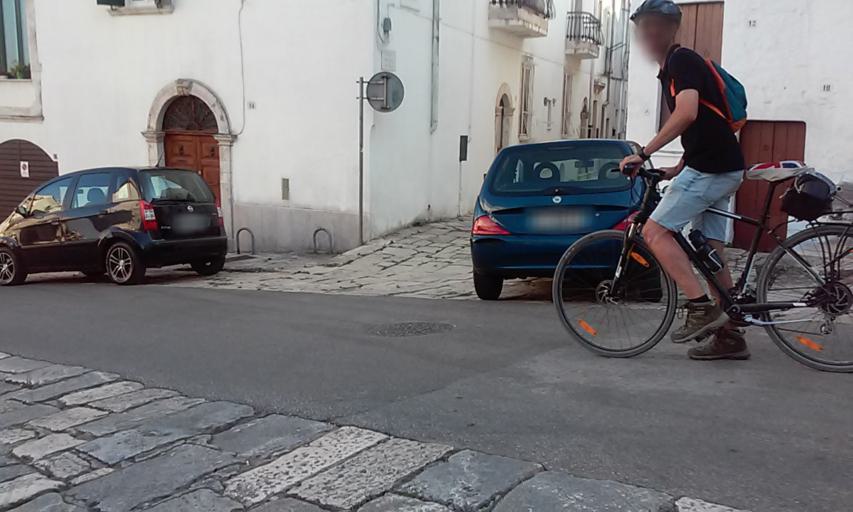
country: IT
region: Apulia
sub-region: Provincia di Brindisi
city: Ceglie Messapica
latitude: 40.6461
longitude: 17.5192
